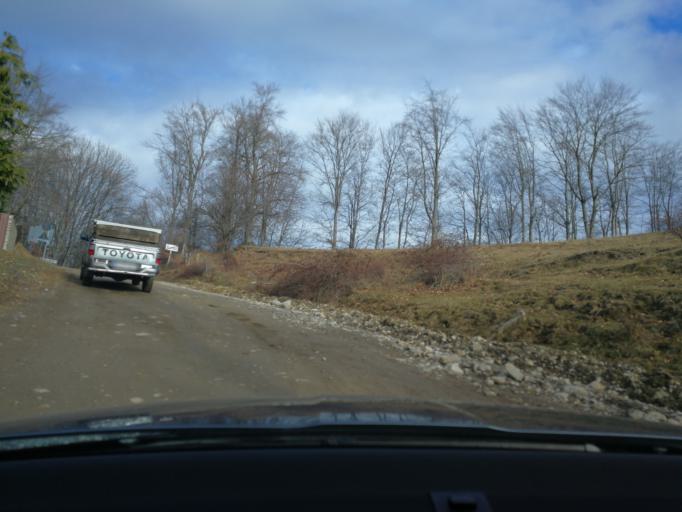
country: RO
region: Prahova
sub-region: Comuna Adunati
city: Ocina de Sus
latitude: 45.1741
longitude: 25.5634
